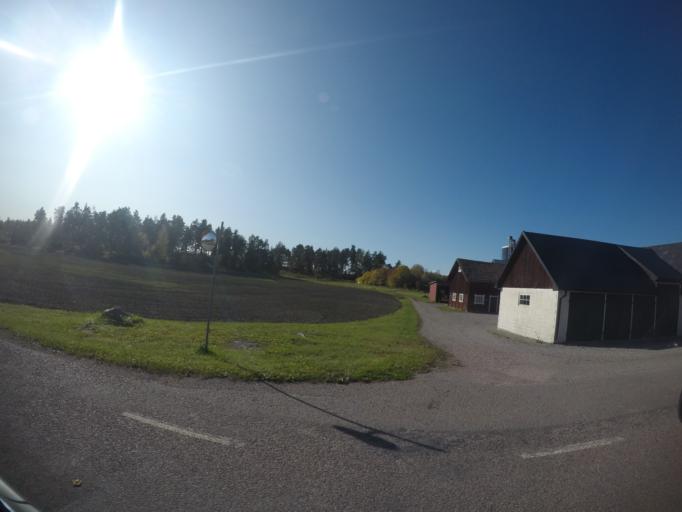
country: SE
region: Vaestmanland
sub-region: Vasteras
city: Vasteras
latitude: 59.5538
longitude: 16.4234
